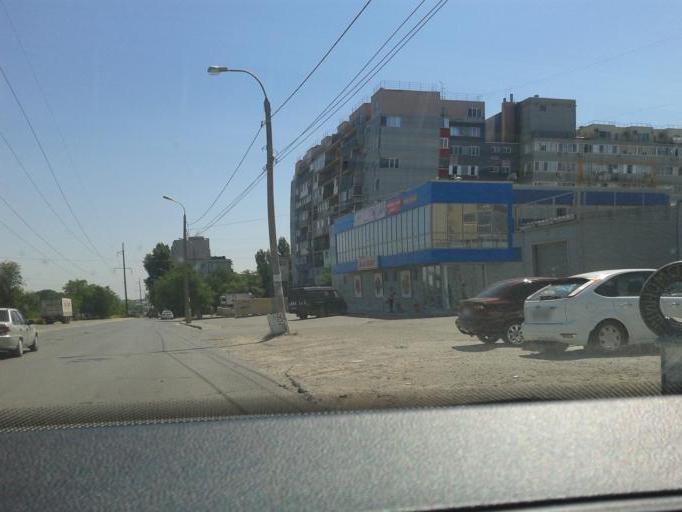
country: RU
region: Volgograd
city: Gorodishche
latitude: 48.7675
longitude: 44.4887
